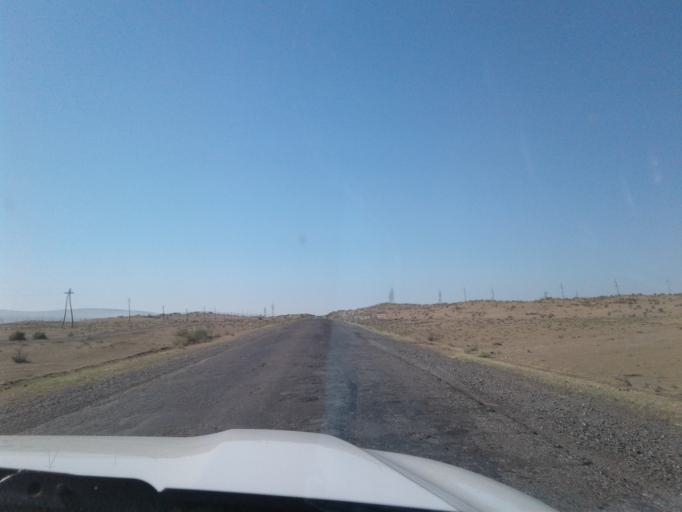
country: TM
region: Mary
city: Yoloeten
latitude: 36.5651
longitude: 62.5406
